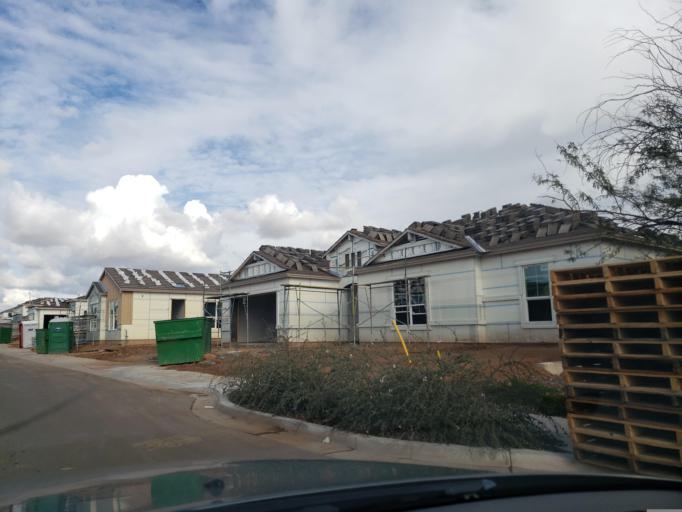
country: US
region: Arizona
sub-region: Maricopa County
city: Paradise Valley
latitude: 33.6449
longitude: -111.9694
